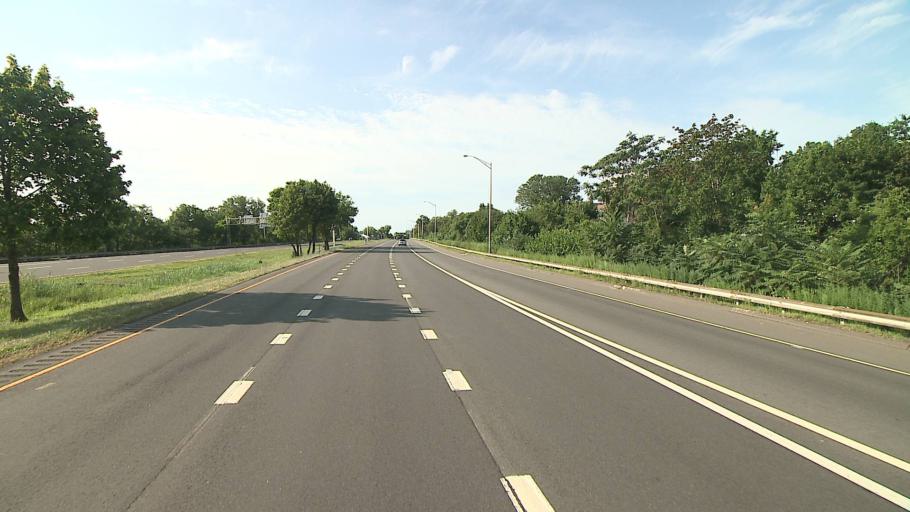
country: US
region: Connecticut
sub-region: Fairfield County
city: Norwalk
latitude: 41.1149
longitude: -73.4192
